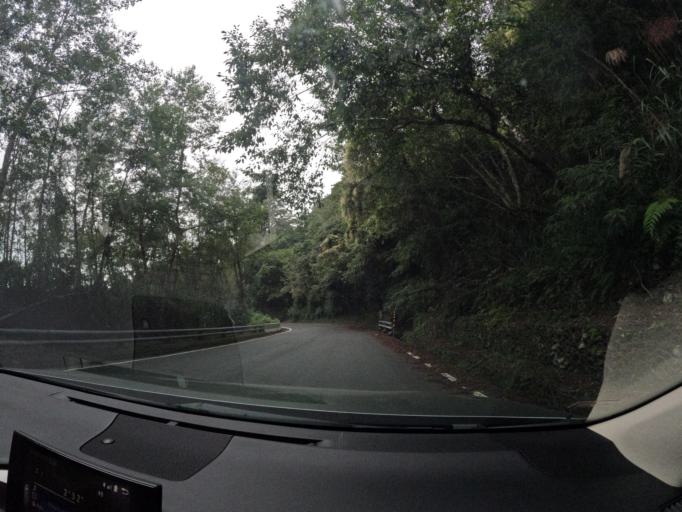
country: TW
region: Taiwan
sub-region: Taitung
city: Taitung
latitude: 23.2409
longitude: 120.9840
